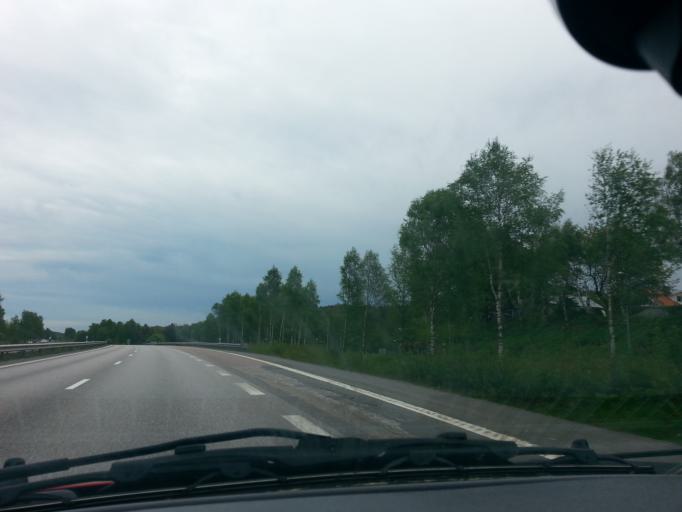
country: SE
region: Vaestra Goetaland
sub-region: Lerums Kommun
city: Lerum
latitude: 57.7727
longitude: 12.2895
